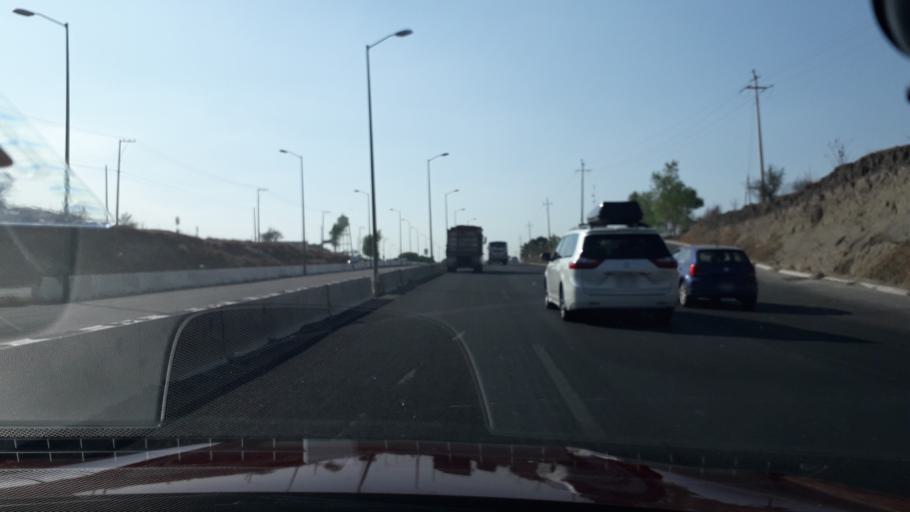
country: MX
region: Puebla
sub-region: Puebla
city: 18 de Marzo
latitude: 18.9739
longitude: -98.2098
